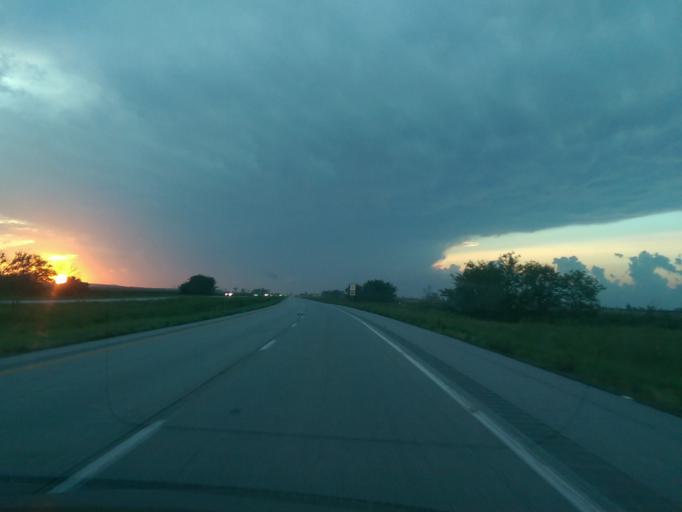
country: US
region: Iowa
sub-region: Fremont County
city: Hamburg
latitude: 40.6079
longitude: -95.6843
